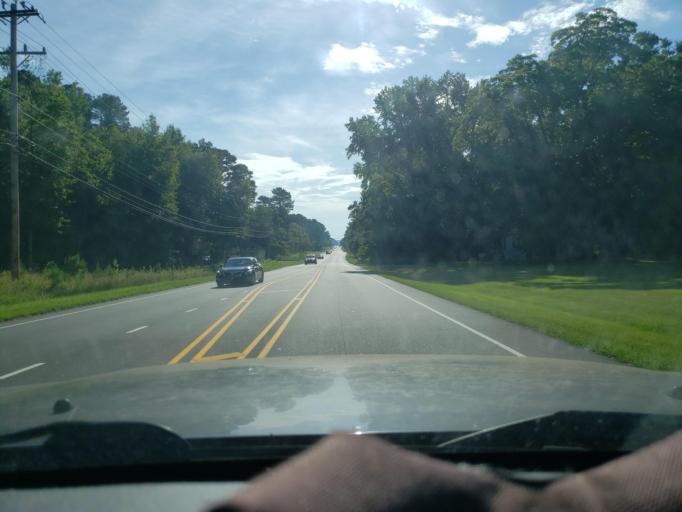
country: US
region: North Carolina
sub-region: Durham County
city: Gorman
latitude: 35.9755
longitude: -78.7859
